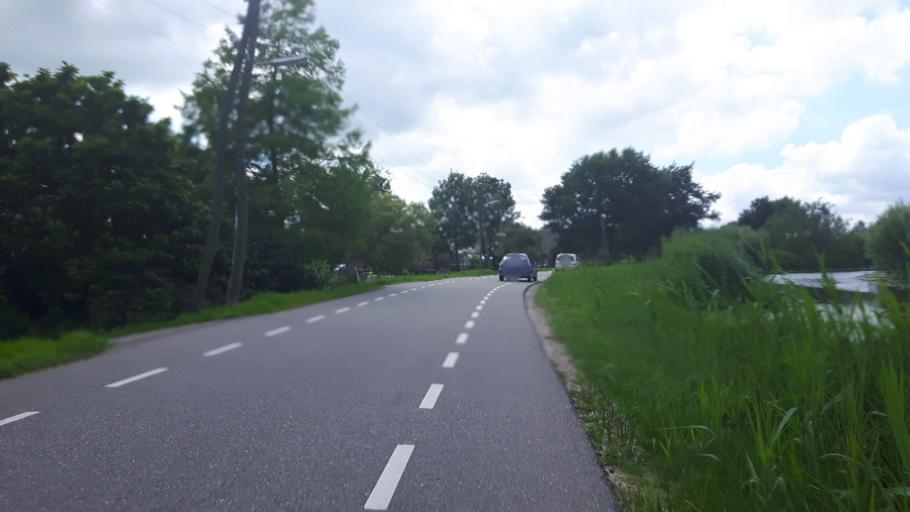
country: NL
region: South Holland
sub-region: Gemeente Vlist
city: Vlist
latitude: 51.9793
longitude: 4.8181
